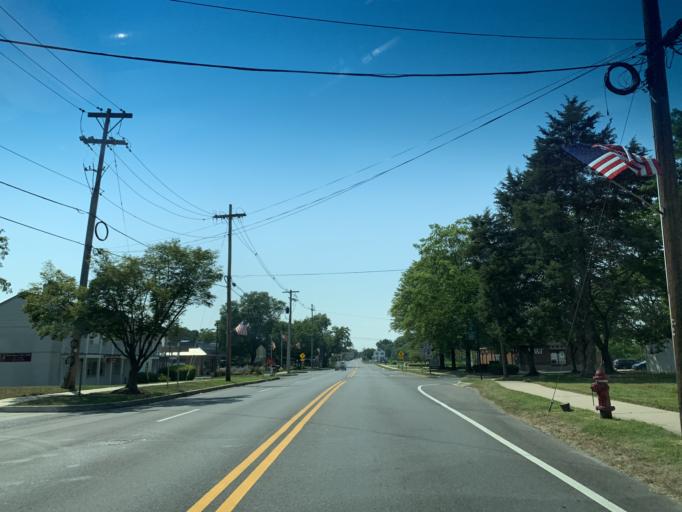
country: US
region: Maryland
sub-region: Montgomery County
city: Poolesville
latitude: 39.1442
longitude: -77.4099
